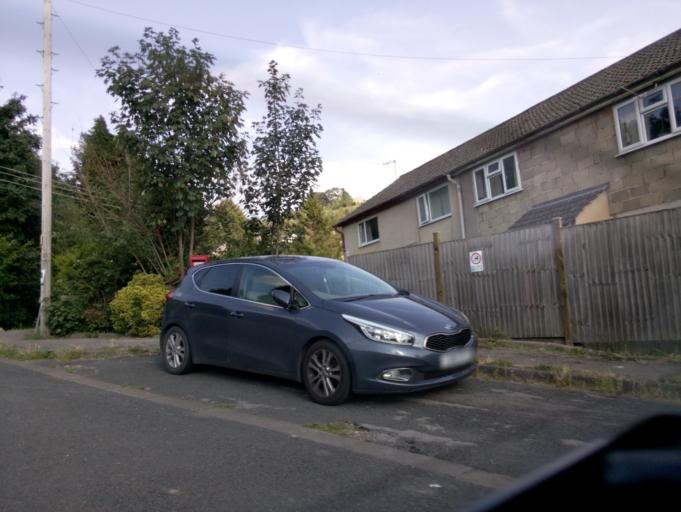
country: GB
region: England
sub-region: Gloucestershire
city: Stroud
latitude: 51.7367
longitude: -2.2285
